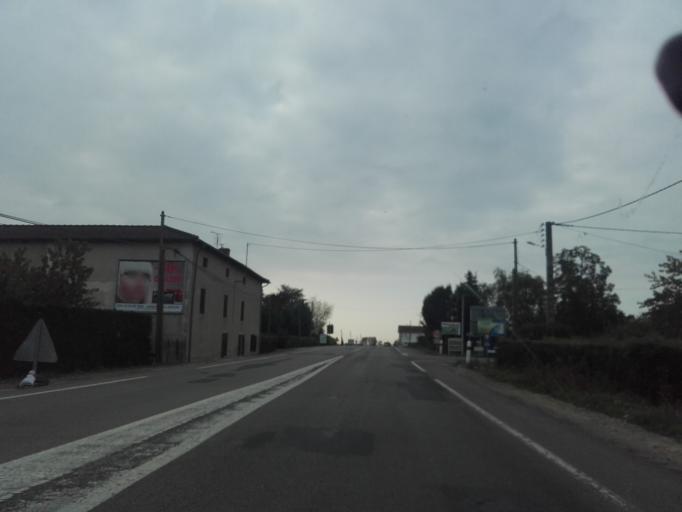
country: FR
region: Bourgogne
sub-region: Departement de Saone-et-Loire
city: Creches-sur-Saone
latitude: 46.2376
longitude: 4.7868
